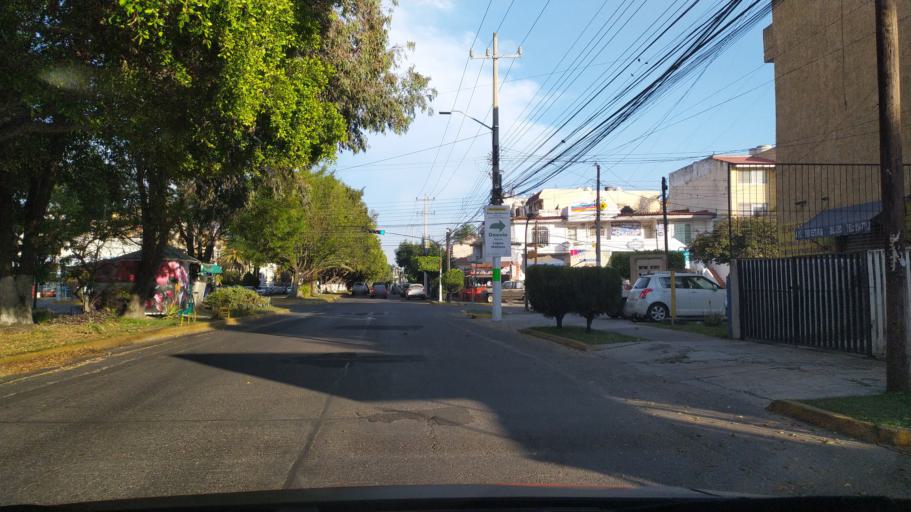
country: MX
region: Jalisco
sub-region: Tlajomulco de Zuniga
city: La Tijera
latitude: 20.6270
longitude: -103.4253
